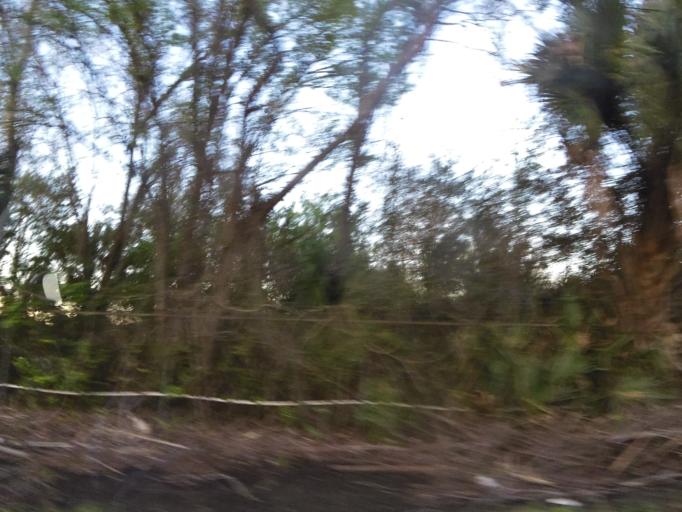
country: US
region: Florida
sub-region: Duval County
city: Jacksonville
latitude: 30.3470
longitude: -81.7088
